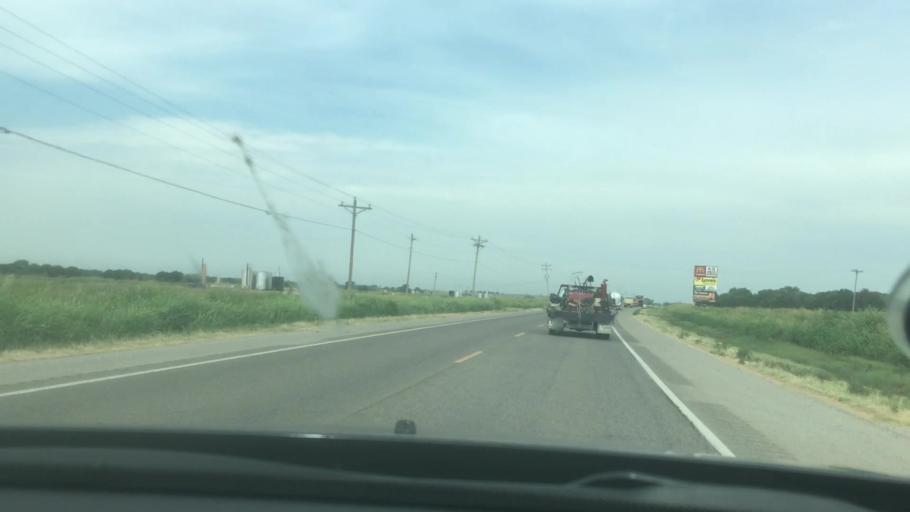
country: US
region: Oklahoma
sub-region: Garvin County
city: Lindsay
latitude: 34.8220
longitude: -97.5190
